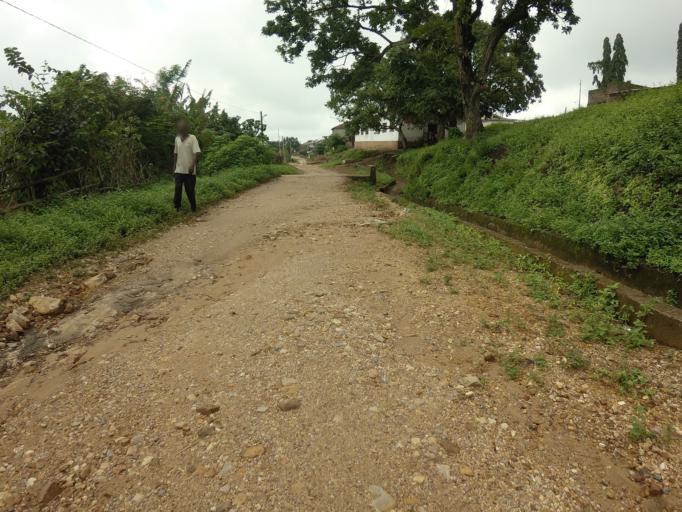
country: TG
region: Plateaux
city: Kpalime
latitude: 6.8448
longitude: 0.4356
